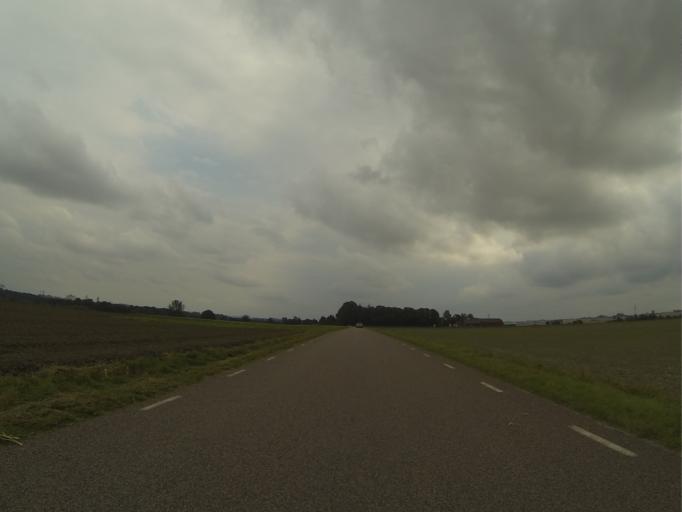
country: SE
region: Skane
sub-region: Lunds Kommun
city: Lund
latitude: 55.7766
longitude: 13.2200
